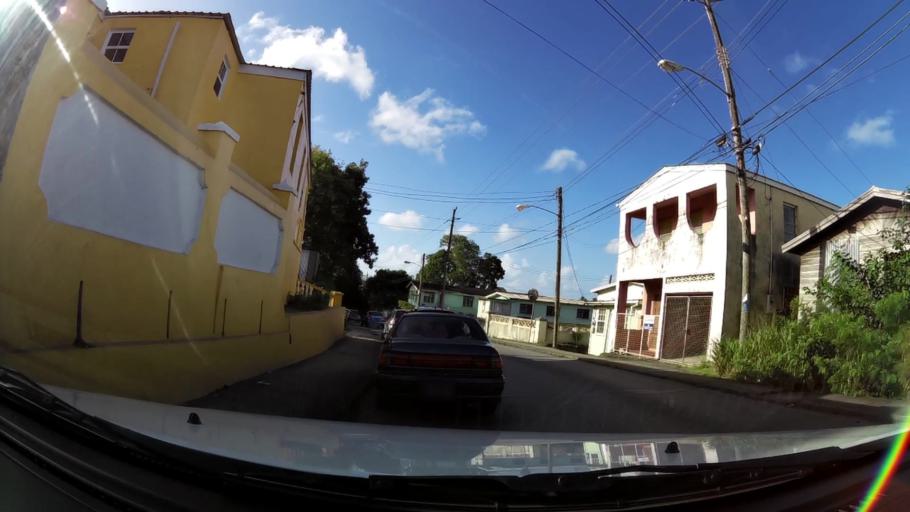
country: BB
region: Saint Michael
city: Bridgetown
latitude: 13.1061
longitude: -59.5970
